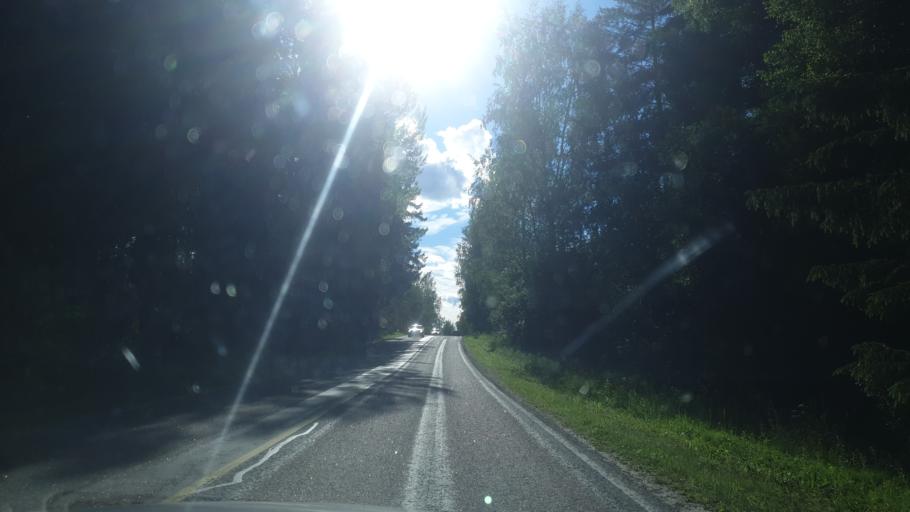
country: FI
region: Southern Savonia
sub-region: Mikkeli
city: Pertunmaa
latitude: 61.5233
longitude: 26.5163
